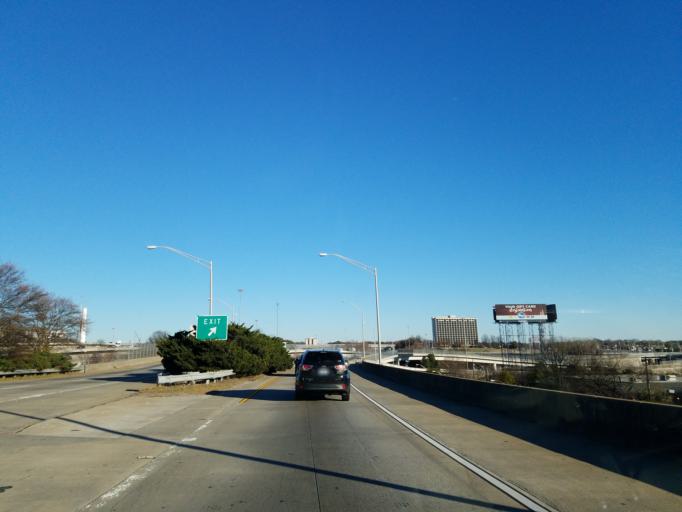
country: US
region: Georgia
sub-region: Fulton County
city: Atlanta
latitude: 33.7449
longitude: -84.3956
